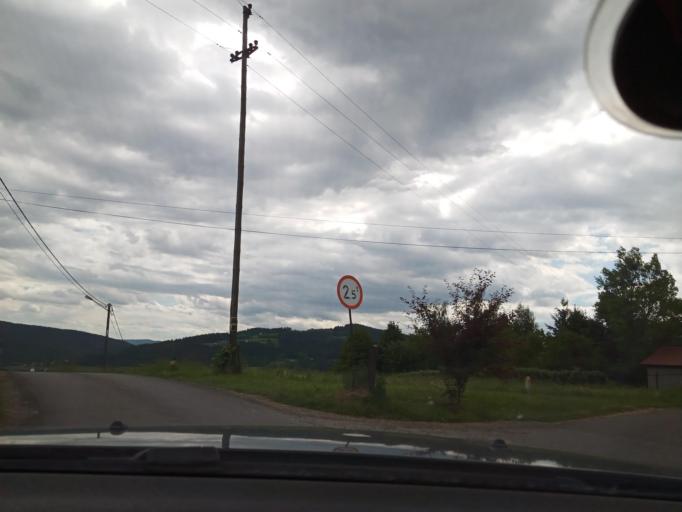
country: PL
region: Lesser Poland Voivodeship
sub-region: Powiat limanowski
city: Tymbark
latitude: 49.7716
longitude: 20.3364
